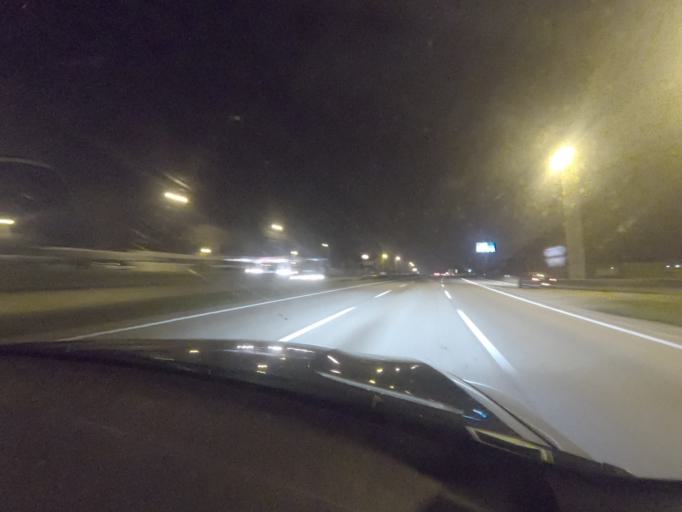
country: PT
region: Lisbon
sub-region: Azambuja
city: Aveiras de Cima
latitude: 39.1230
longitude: -8.9079
